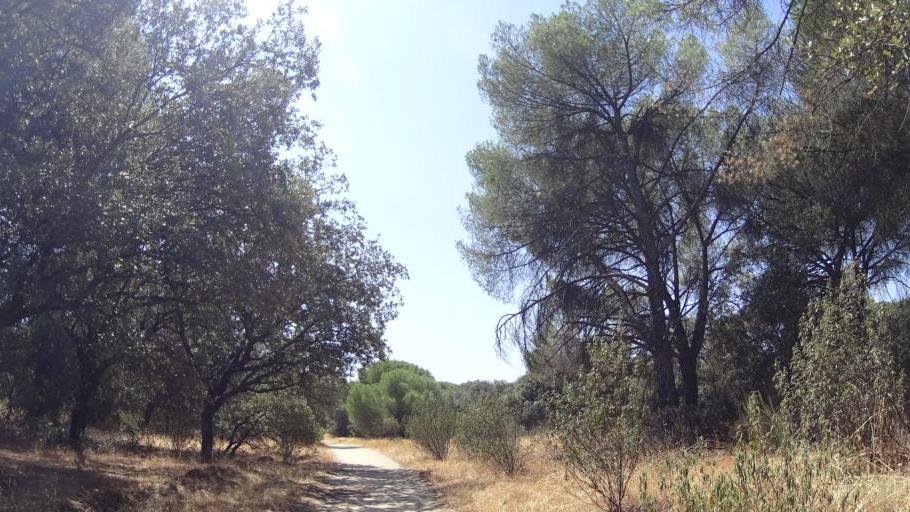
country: ES
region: Madrid
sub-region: Provincia de Madrid
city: Boadilla del Monte
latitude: 40.4370
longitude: -3.8730
